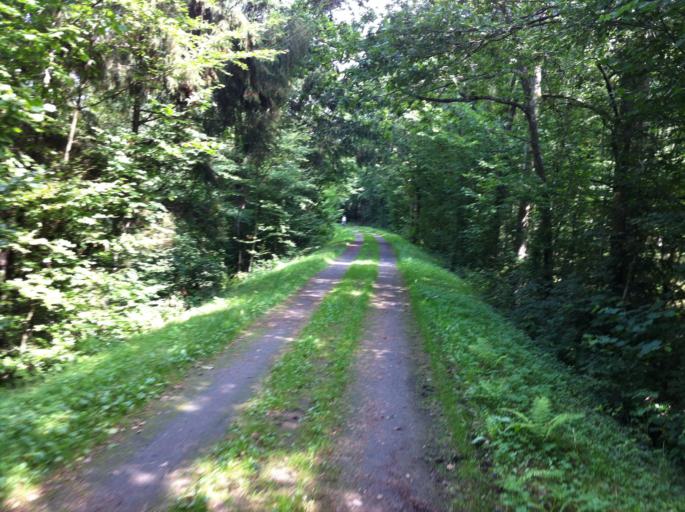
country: SE
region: Skane
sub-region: Hassleholms Kommun
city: Vinslov
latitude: 55.9441
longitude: 13.8426
